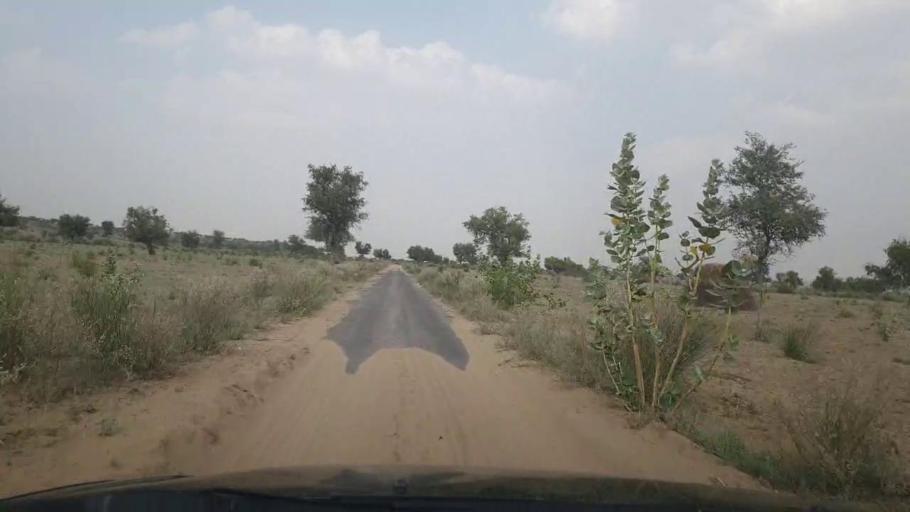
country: PK
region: Sindh
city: Islamkot
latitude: 24.9104
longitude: 70.5603
